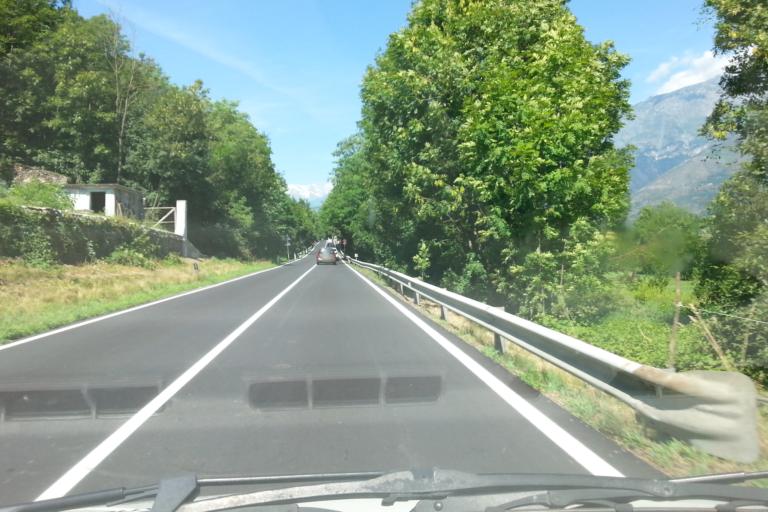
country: IT
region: Piedmont
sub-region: Provincia di Torino
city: San Didero
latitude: 45.1210
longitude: 7.2035
